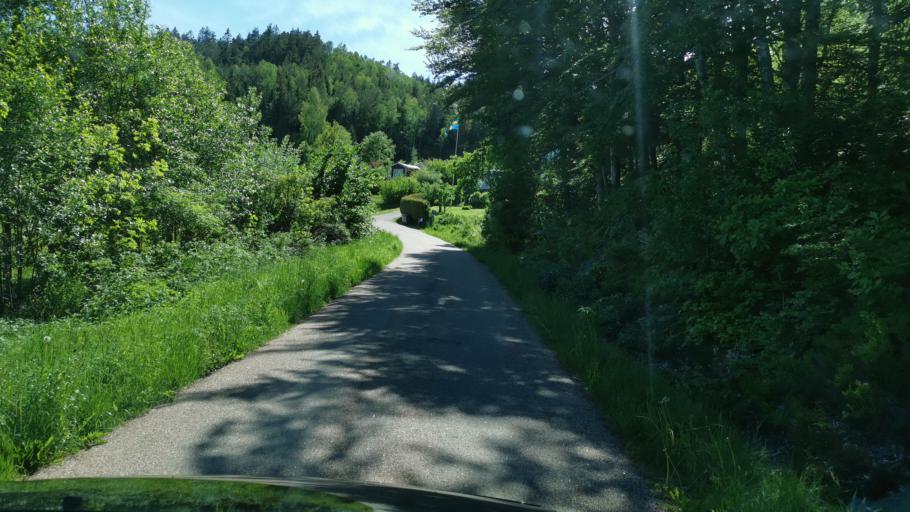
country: SE
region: Vaestra Goetaland
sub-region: Orust
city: Henan
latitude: 58.2756
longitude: 11.6379
